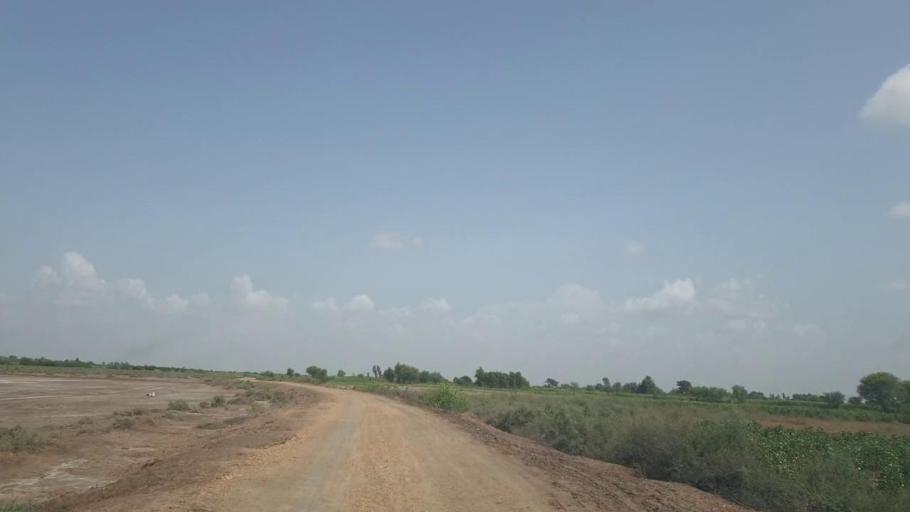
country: PK
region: Sindh
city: Tando Bago
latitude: 24.7546
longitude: 69.1725
